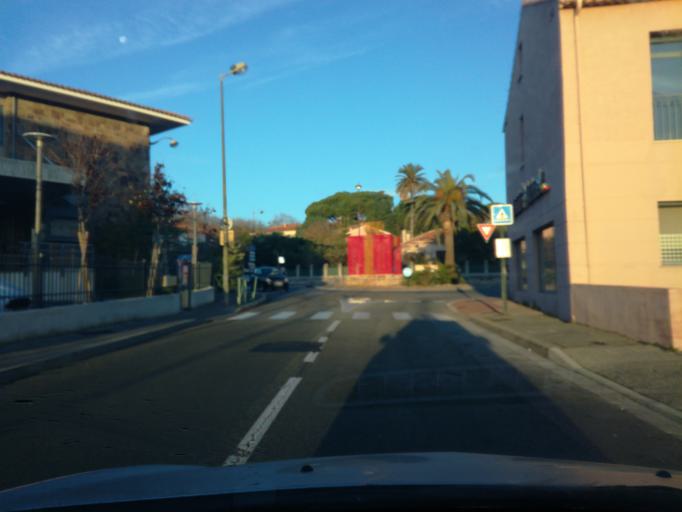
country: FR
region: Provence-Alpes-Cote d'Azur
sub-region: Departement du Var
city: Frejus
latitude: 43.4332
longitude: 6.7412
